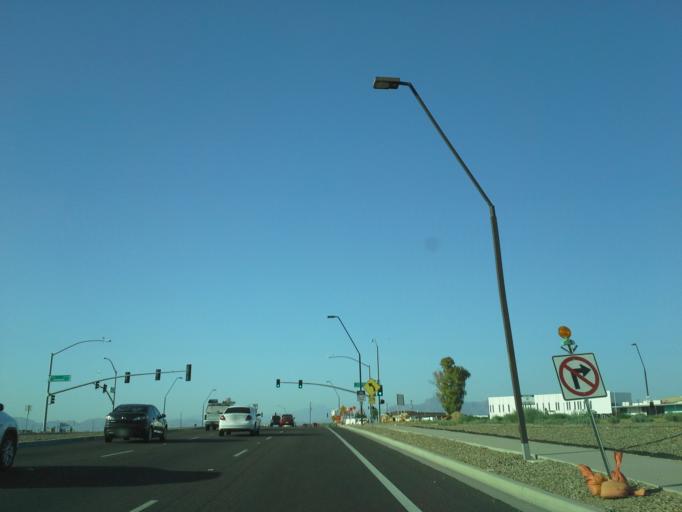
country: US
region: Arizona
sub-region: Maricopa County
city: Queen Creek
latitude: 33.2604
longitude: -111.6366
